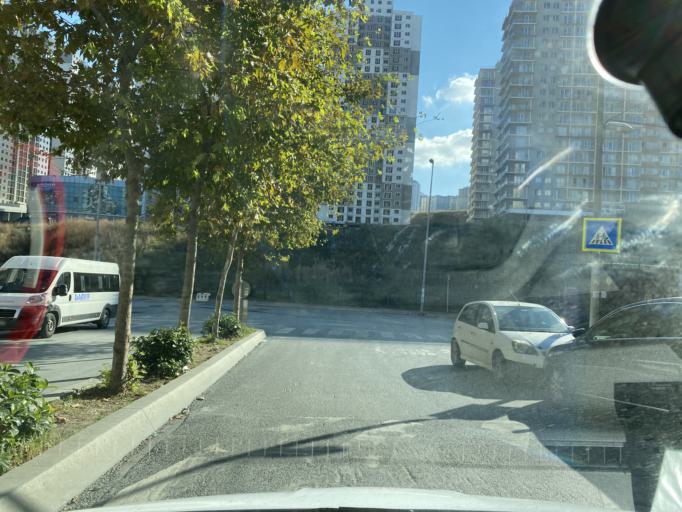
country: TR
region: Istanbul
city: Esenyurt
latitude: 41.0281
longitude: 28.6523
